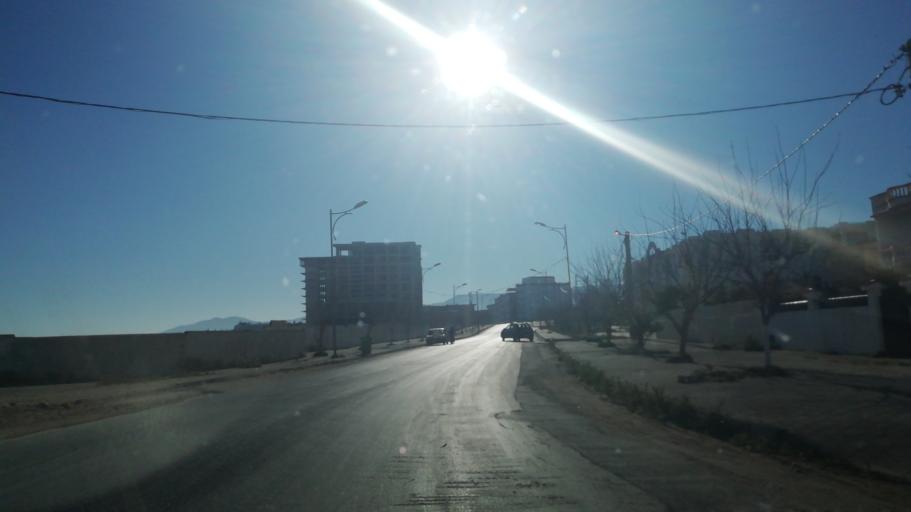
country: DZ
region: Oran
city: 'Ain el Turk
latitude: 35.7551
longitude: -0.7862
